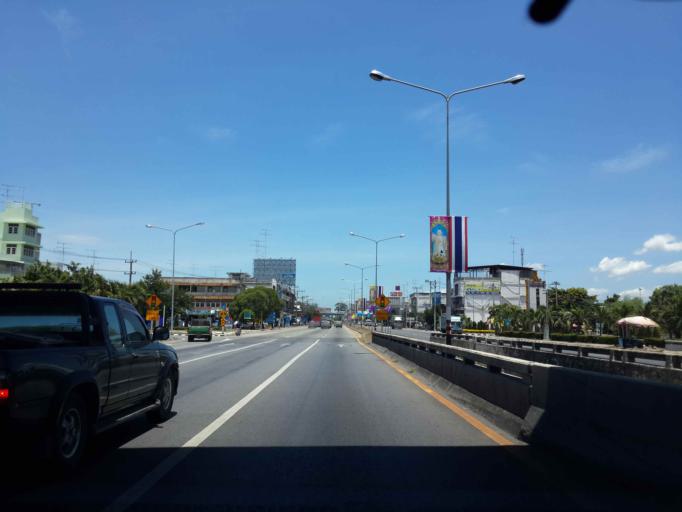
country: TH
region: Phetchaburi
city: Tha Yang
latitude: 12.9712
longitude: 99.8992
